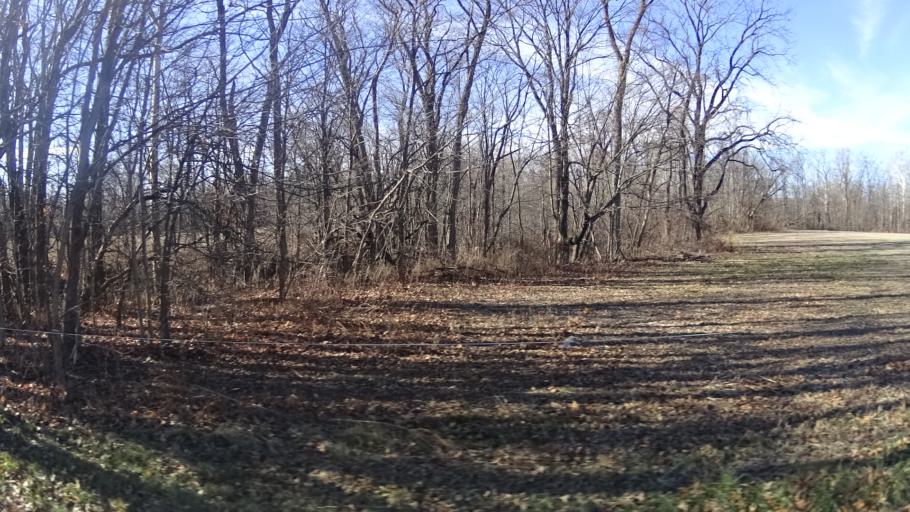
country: US
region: Ohio
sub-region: Huron County
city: Wakeman
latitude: 41.3071
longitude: -82.3432
